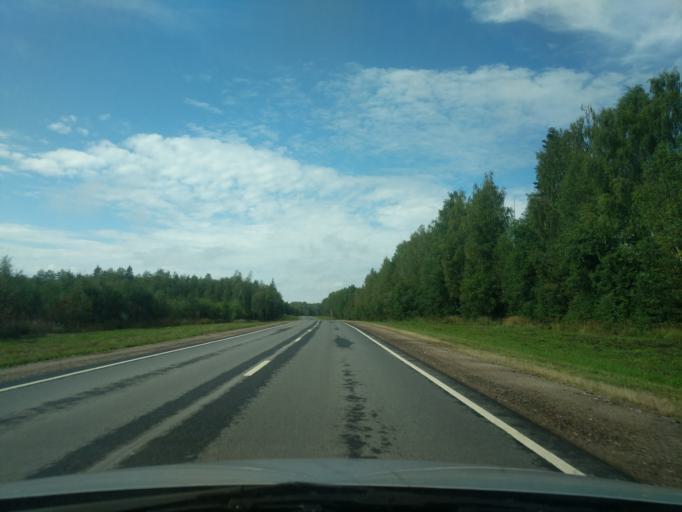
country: RU
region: Kostroma
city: Sudislavl'
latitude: 57.8355
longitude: 41.8706
